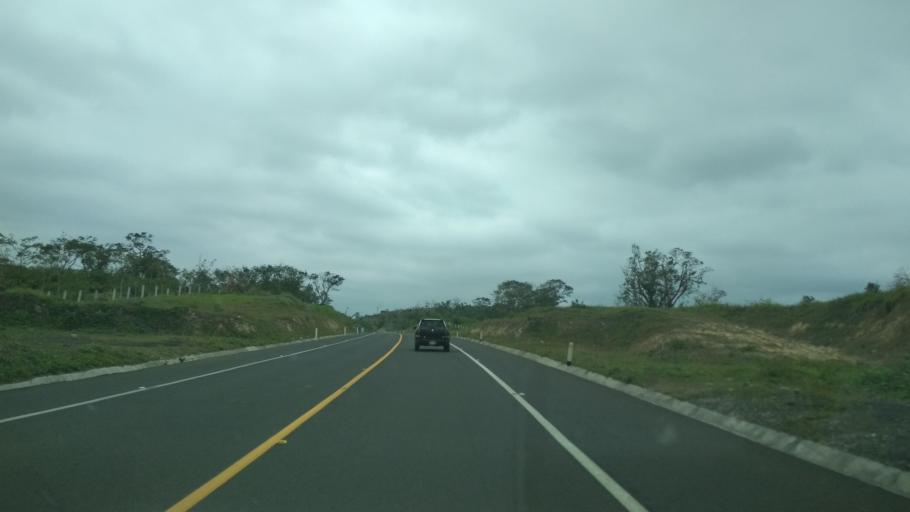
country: MX
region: Veracruz
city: Agua Dulce
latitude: 20.4296
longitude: -97.2272
